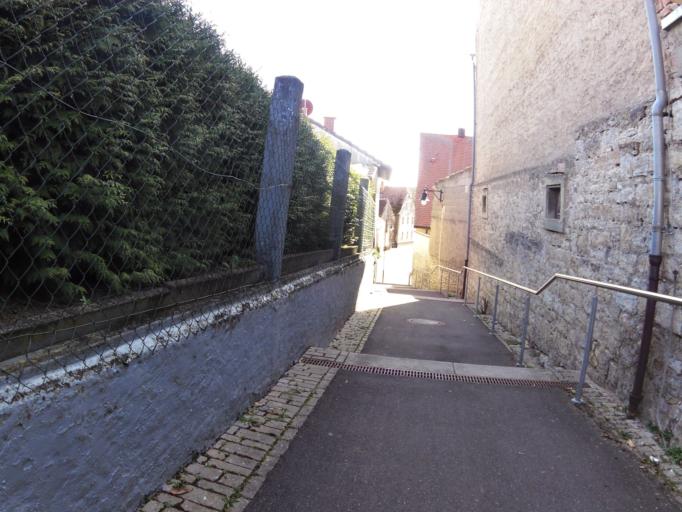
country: DE
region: Bavaria
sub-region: Regierungsbezirk Unterfranken
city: Biebelried
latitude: 49.7987
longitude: 10.1060
